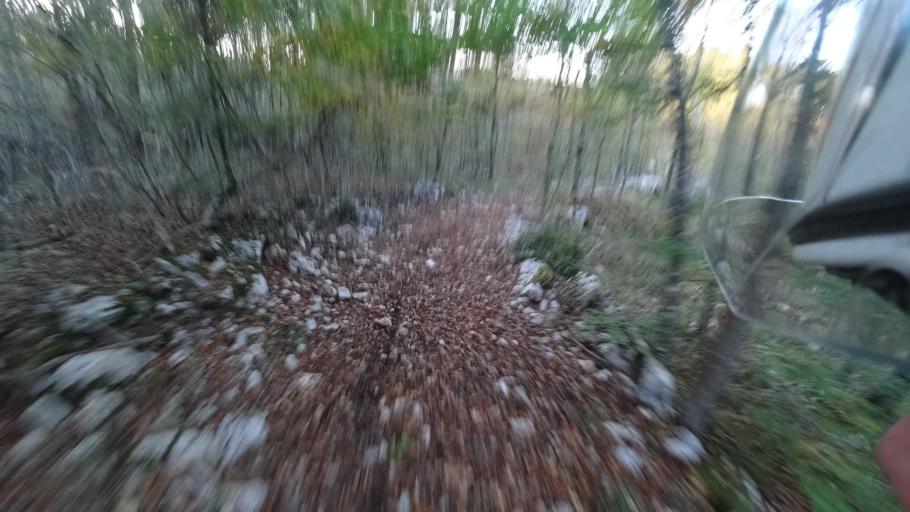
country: HR
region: Primorsko-Goranska
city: Kastav
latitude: 45.4106
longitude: 14.3212
